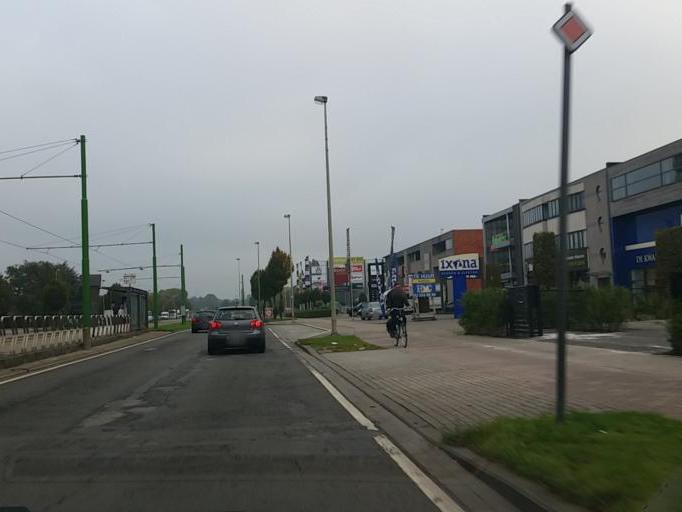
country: BE
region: Flanders
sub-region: Provincie Antwerpen
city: Schoten
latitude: 51.2545
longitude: 4.4594
